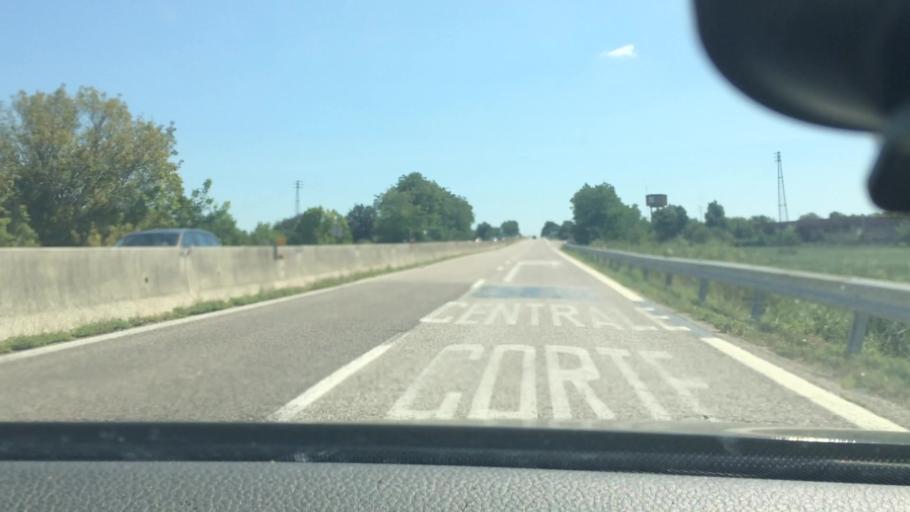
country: IT
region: Emilia-Romagna
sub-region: Provincia di Ferrara
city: Massa Fiscaglia
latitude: 44.7433
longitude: 12.0182
